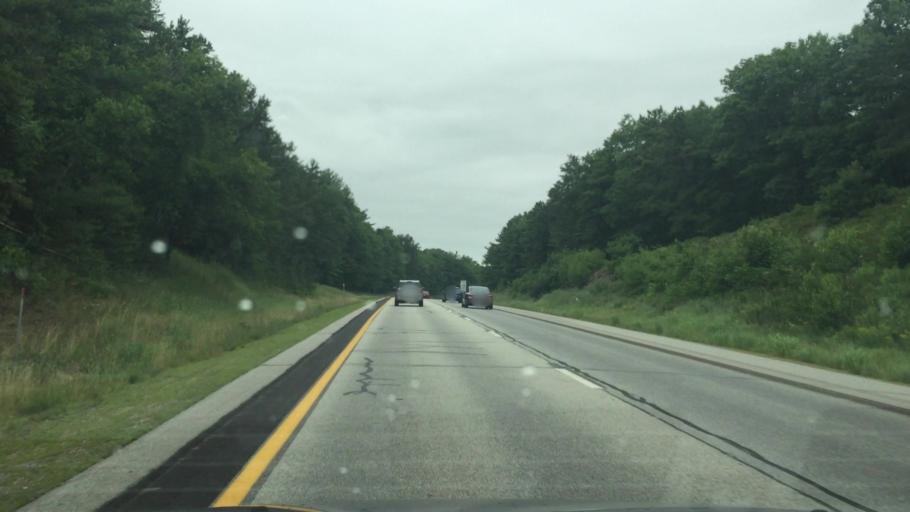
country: US
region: New Hampshire
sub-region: Merrimack County
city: Boscawen
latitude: 43.3386
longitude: -71.6120
